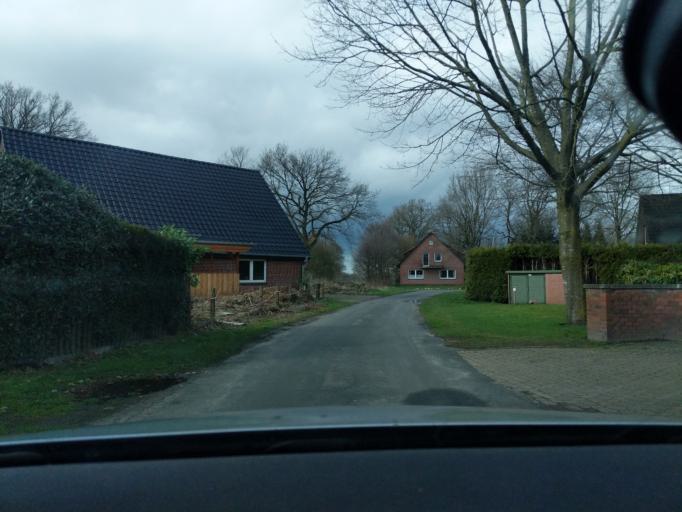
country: DE
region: Lower Saxony
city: Heinbockel
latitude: 53.5757
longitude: 9.3272
